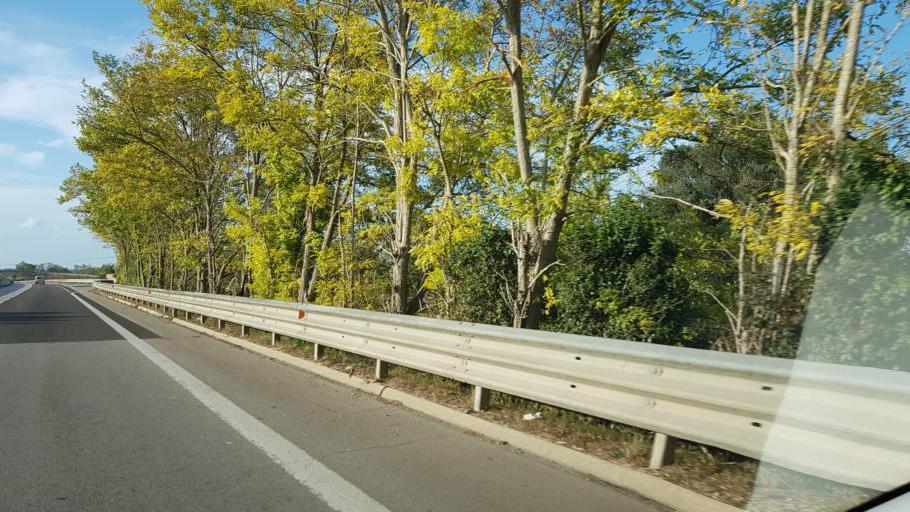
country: IT
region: Apulia
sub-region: Provincia di Brindisi
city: Francavilla Fontana
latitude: 40.5392
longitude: 17.6068
